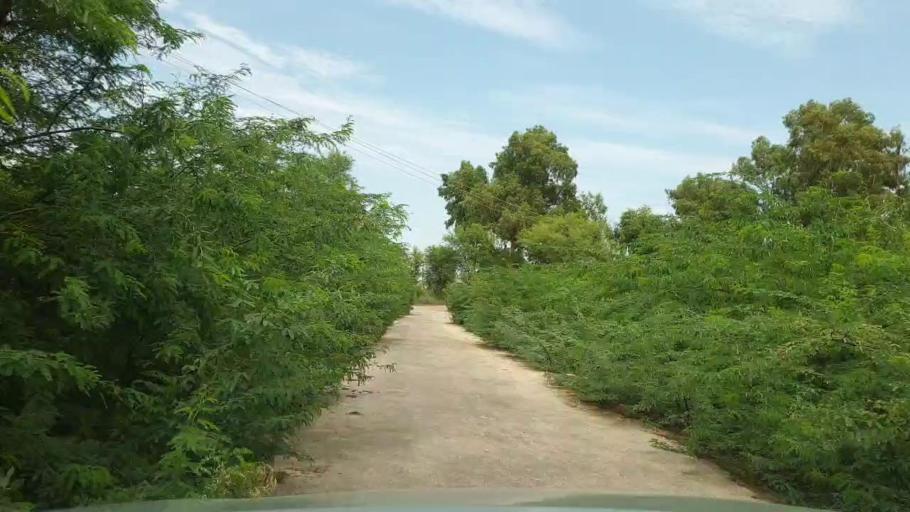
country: PK
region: Sindh
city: Bozdar
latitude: 27.0147
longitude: 68.9406
